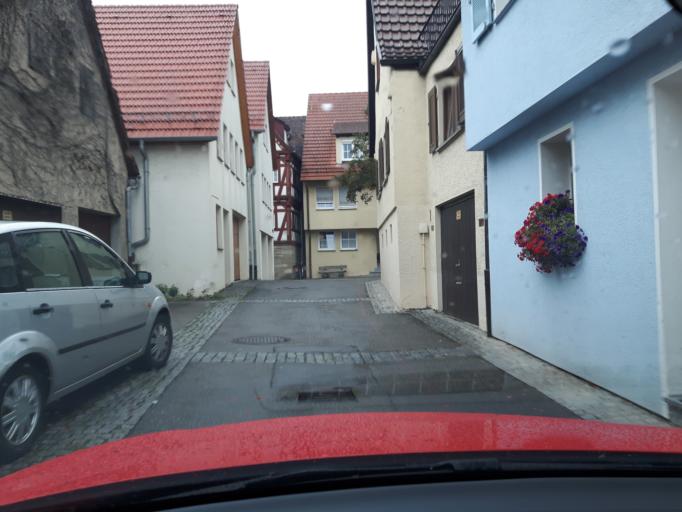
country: DE
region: Baden-Wuerttemberg
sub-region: Regierungsbezirk Stuttgart
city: Bonnigheim
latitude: 49.0408
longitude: 9.0926
